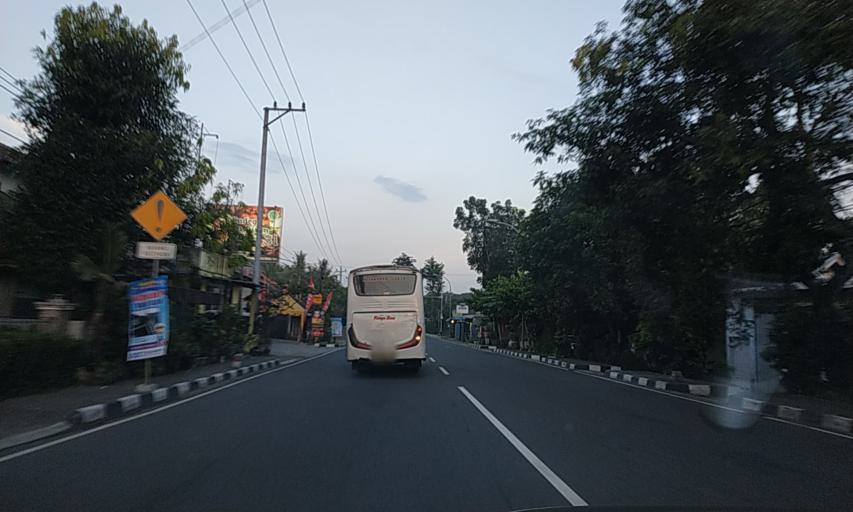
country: ID
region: Daerah Istimewa Yogyakarta
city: Srandakan
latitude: -7.8661
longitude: 110.1600
